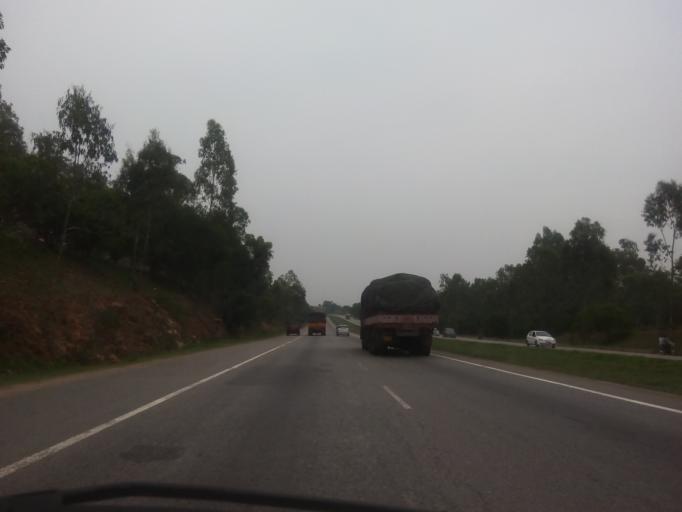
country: IN
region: Karnataka
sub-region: Bangalore Urban
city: Bangalore
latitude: 12.8684
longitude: 77.5049
